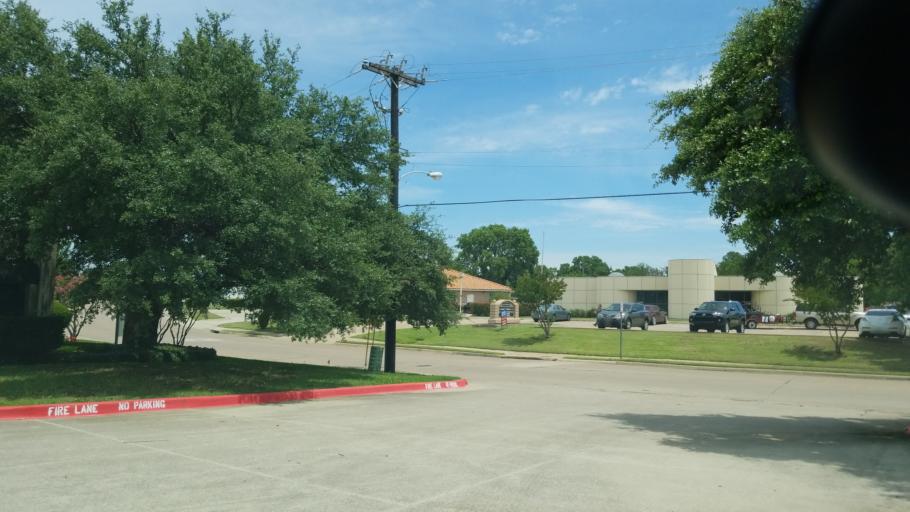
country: US
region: Texas
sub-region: Dallas County
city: Irving
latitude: 32.8397
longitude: -96.9728
